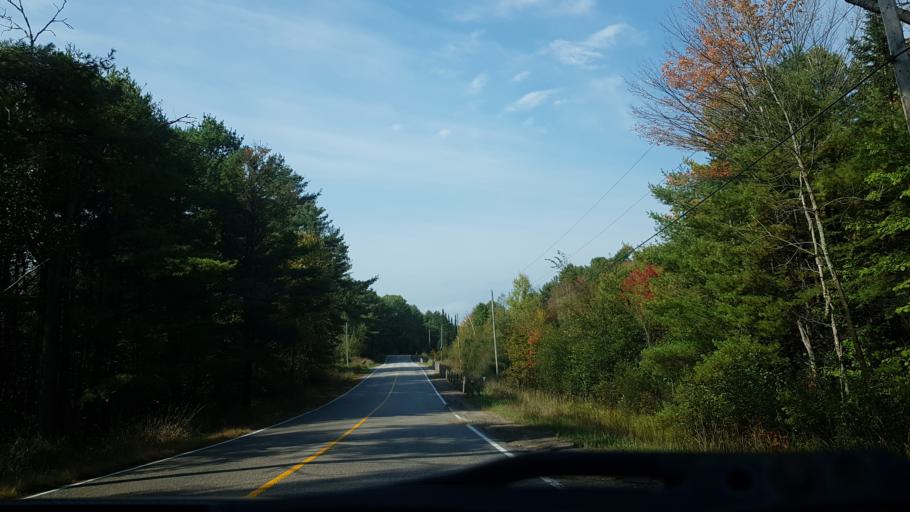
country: CA
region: Ontario
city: Gravenhurst
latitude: 44.7821
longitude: -79.2634
